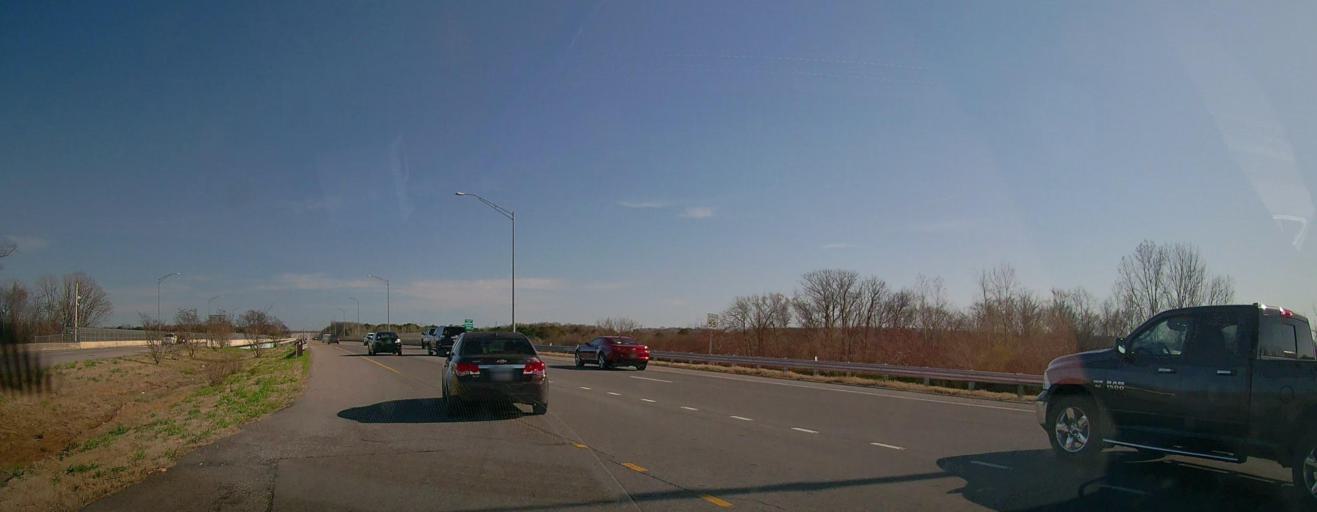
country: US
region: Alabama
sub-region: Lauderdale County
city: East Florence
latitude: 34.8014
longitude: -87.6510
